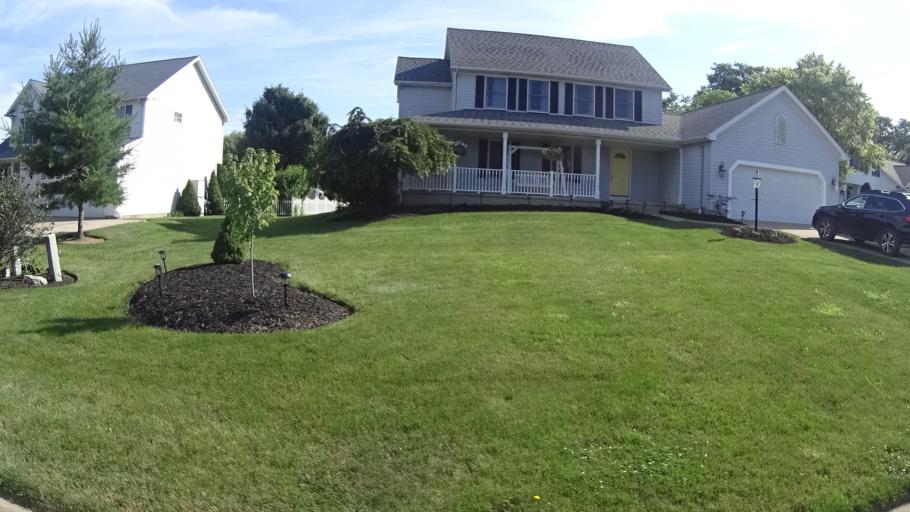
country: US
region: Ohio
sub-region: Erie County
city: Huron
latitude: 41.3824
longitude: -82.5207
